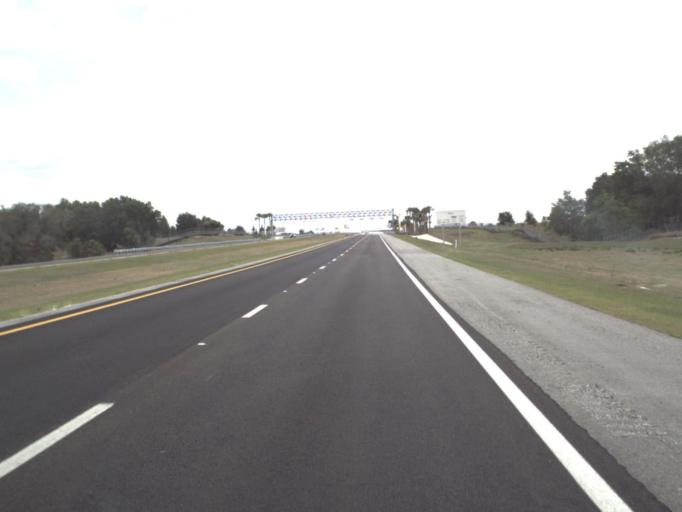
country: US
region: Florida
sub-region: Lake County
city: Mount Plymouth
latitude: 28.7966
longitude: -81.5164
